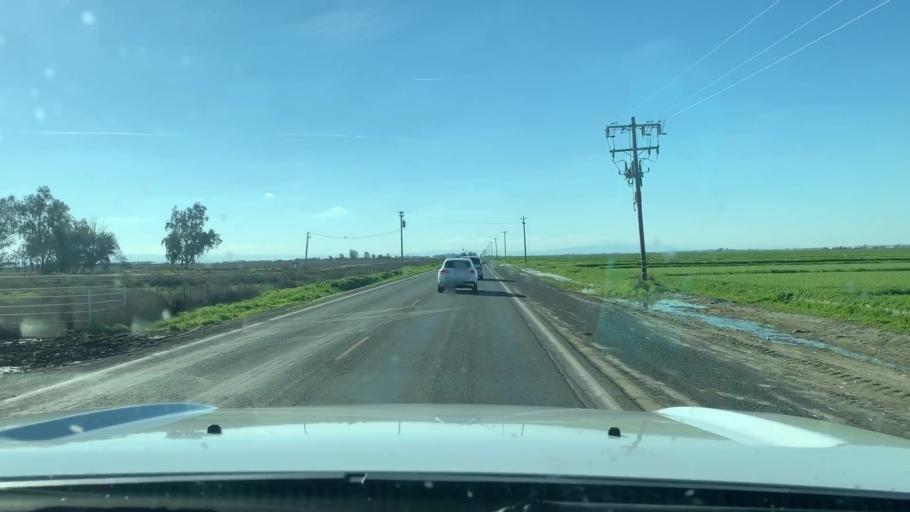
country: US
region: California
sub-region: Kings County
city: Home Garden
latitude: 36.2112
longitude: -119.6584
